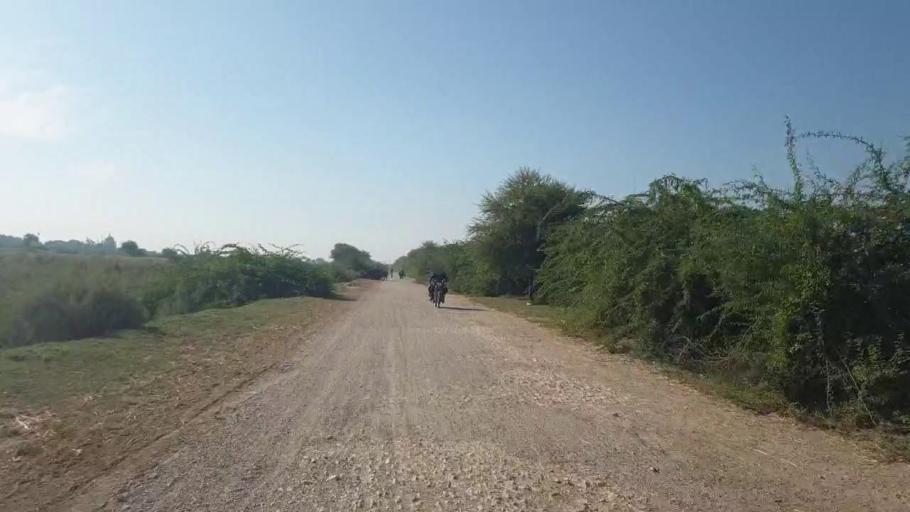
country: PK
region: Sindh
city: Rajo Khanani
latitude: 24.9570
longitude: 68.7959
